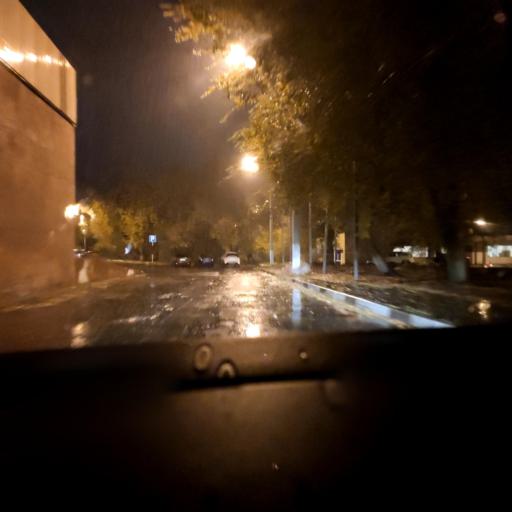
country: RU
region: Voronezj
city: Voronezh
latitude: 51.6447
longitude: 39.1327
